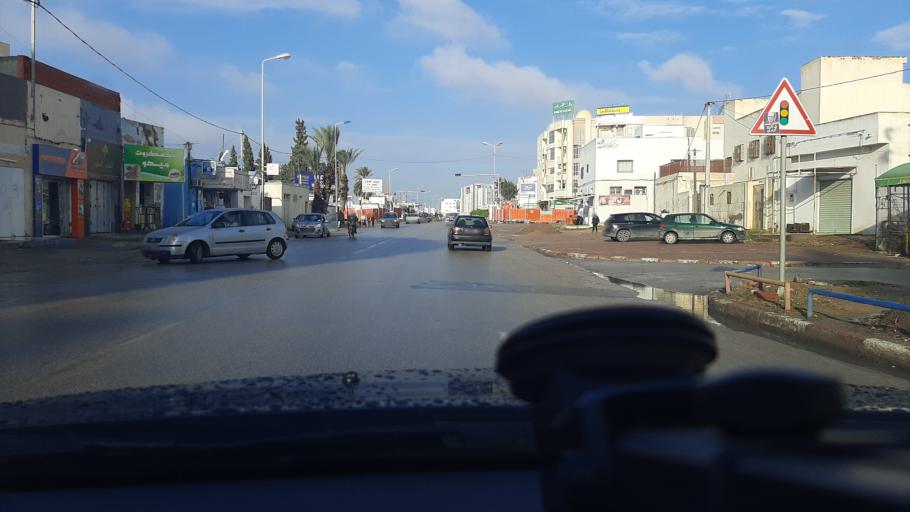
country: TN
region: Safaqis
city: Sfax
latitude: 34.7455
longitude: 10.7273
